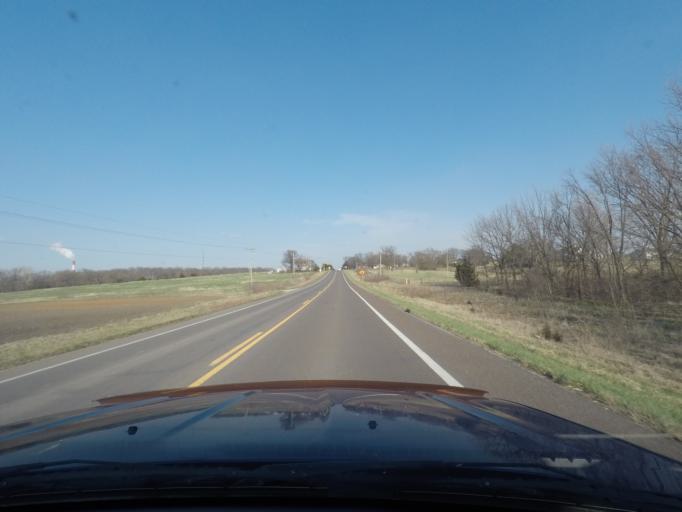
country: US
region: Kansas
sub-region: Douglas County
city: Lawrence
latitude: 39.0006
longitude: -95.2828
